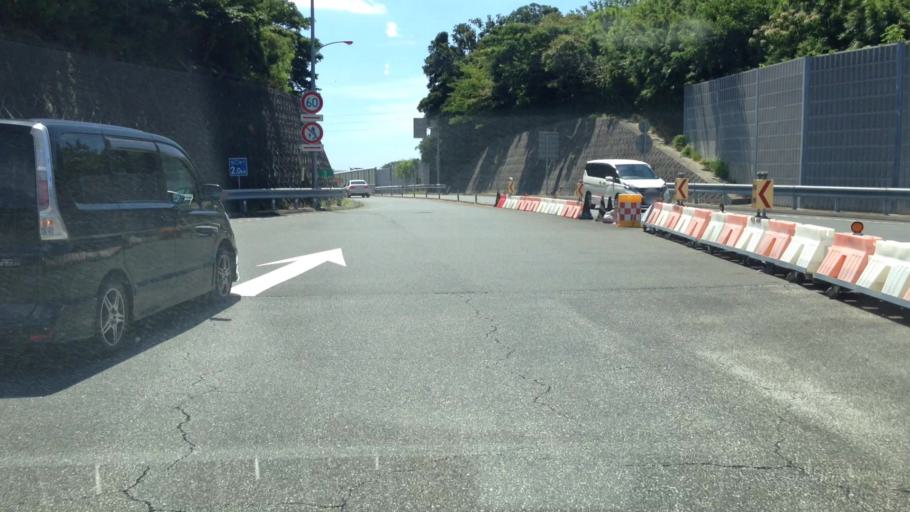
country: JP
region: Kanagawa
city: Yokosuka
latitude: 35.2259
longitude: 139.6384
